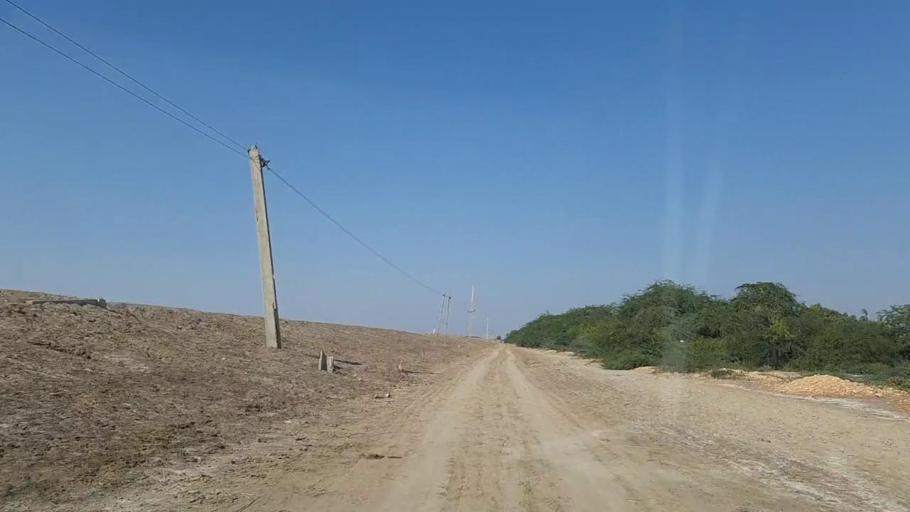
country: PK
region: Sindh
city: Chuhar Jamali
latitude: 24.5394
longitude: 68.0158
